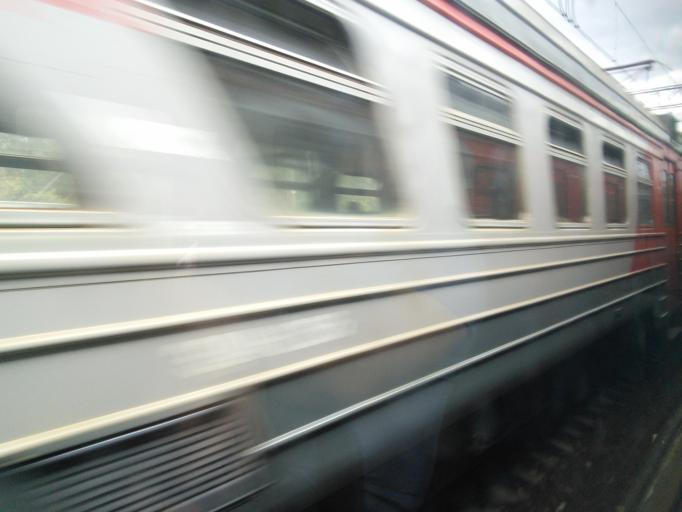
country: RU
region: Moscow
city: Lefortovo
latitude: 55.7779
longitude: 37.7112
